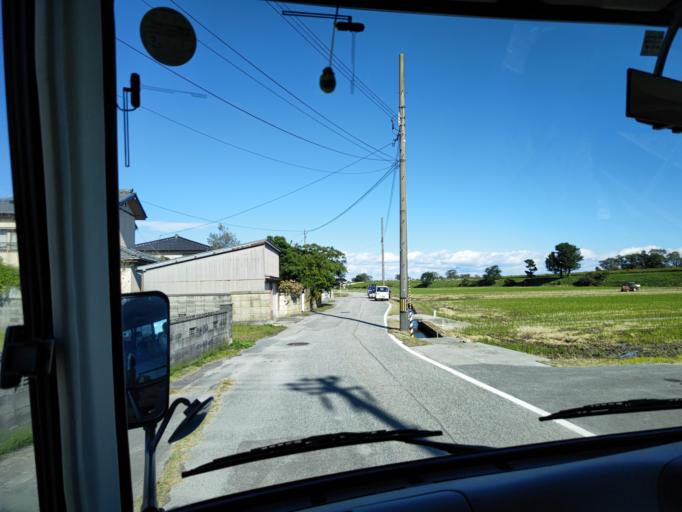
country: JP
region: Toyama
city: Nyuzen
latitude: 36.9085
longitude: 137.4349
